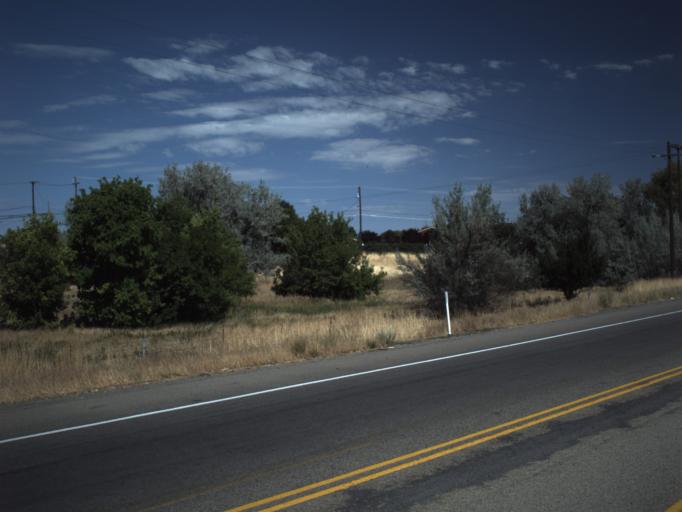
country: US
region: Utah
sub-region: Utah County
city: Spanish Fork
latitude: 40.0920
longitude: -111.6557
